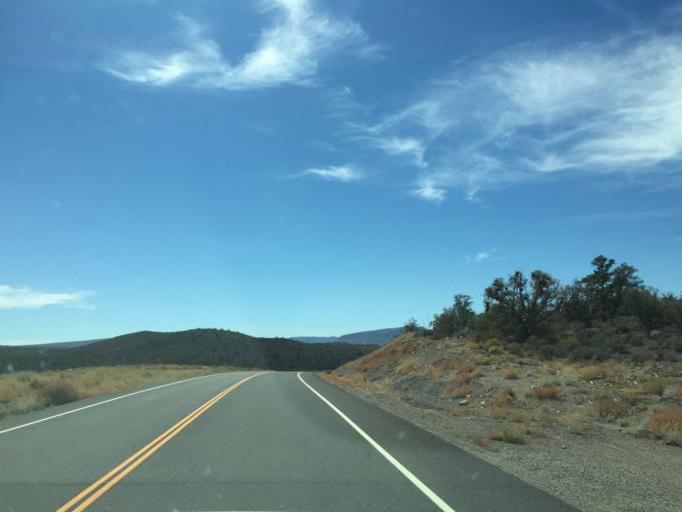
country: US
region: Arizona
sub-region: Mohave County
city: Meadview
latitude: 35.9254
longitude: -113.9093
